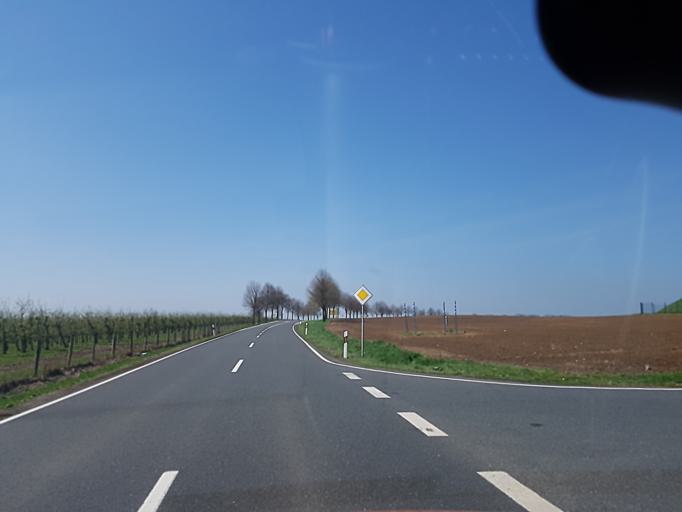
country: DE
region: Saxony
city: Ostrau
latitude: 51.2198
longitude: 12.8652
